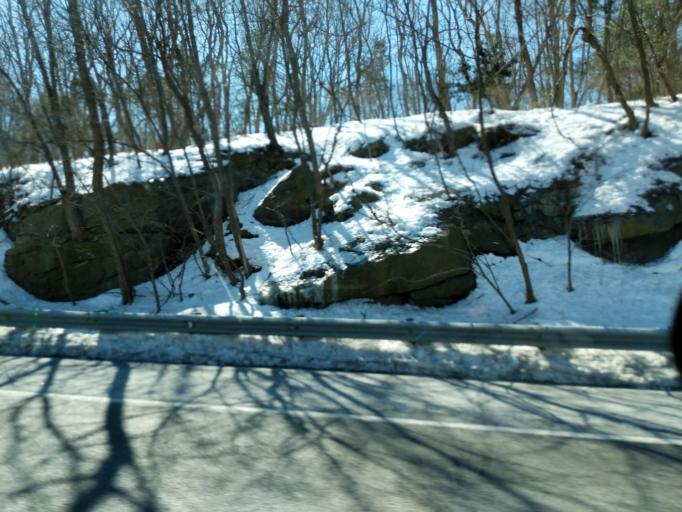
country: US
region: Rhode Island
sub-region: Providence County
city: North Smithfield
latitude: 41.9742
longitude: -71.5264
